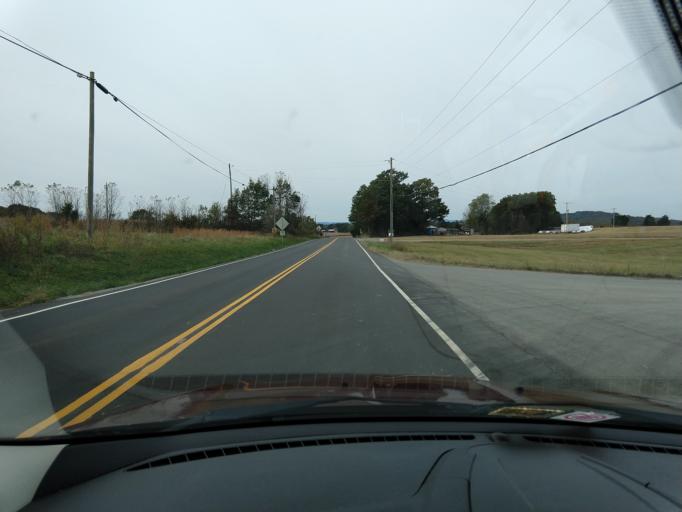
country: US
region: Virginia
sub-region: Franklin County
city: Union Hall
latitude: 36.9865
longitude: -79.7390
